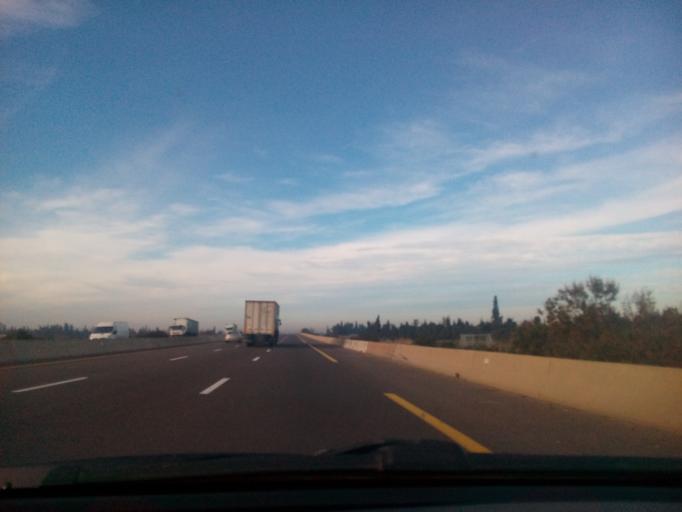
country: DZ
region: Mascara
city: Sig
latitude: 35.6173
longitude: 0.0273
